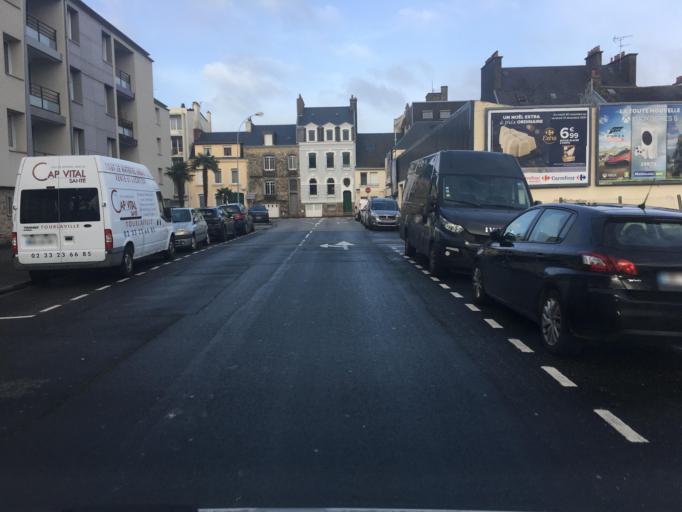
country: FR
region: Lower Normandy
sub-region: Departement de la Manche
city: Cherbourg-Octeville
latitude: 49.6384
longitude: -1.6060
